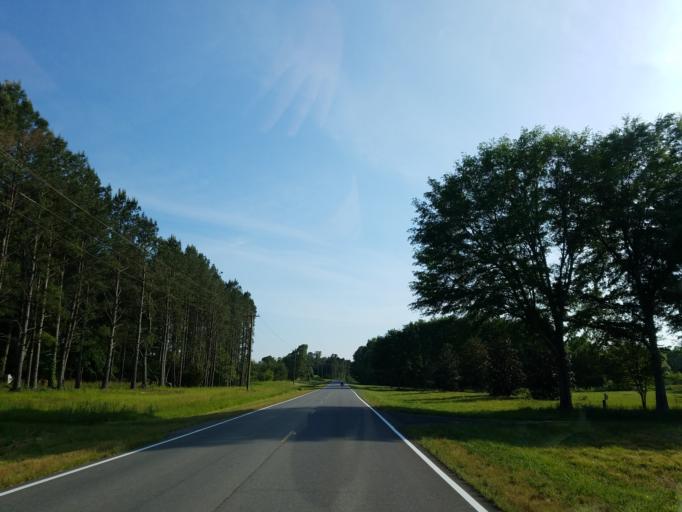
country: US
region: Georgia
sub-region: Chattooga County
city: Trion
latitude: 34.5250
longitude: -85.2169
